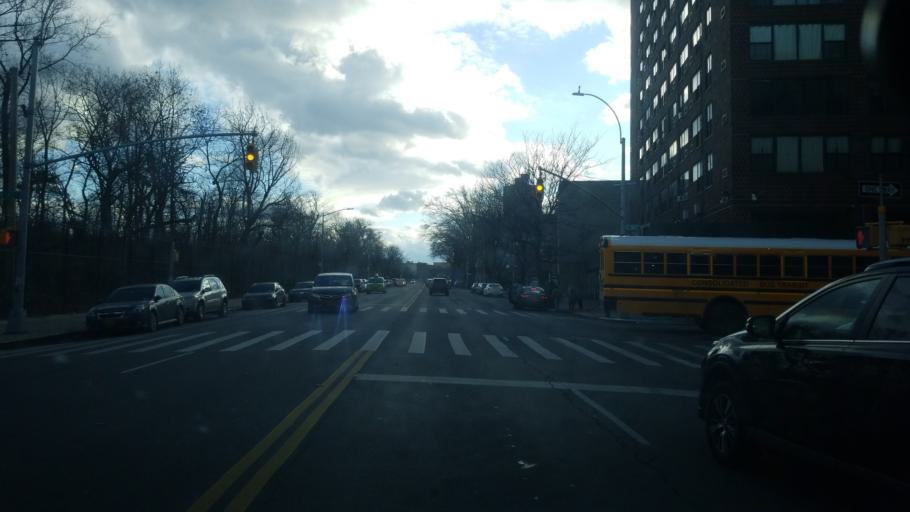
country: US
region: New York
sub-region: Bronx
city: The Bronx
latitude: 40.8513
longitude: -73.8823
